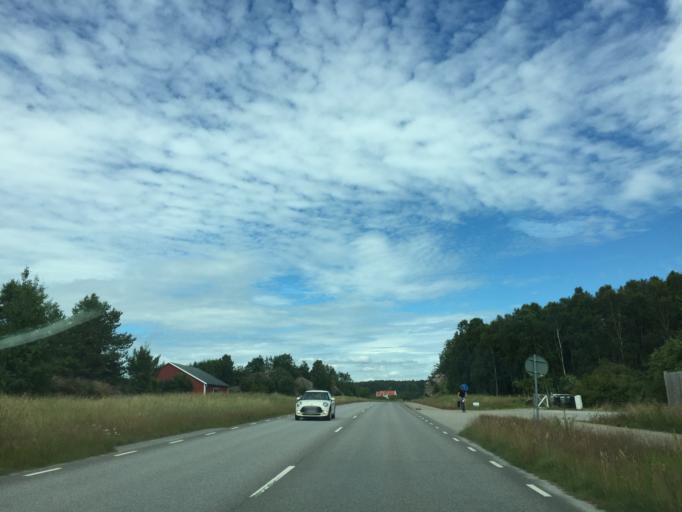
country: SE
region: Vaestra Goetaland
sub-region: Tjorns Kommun
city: Skaerhamn
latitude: 58.0136
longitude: 11.6118
